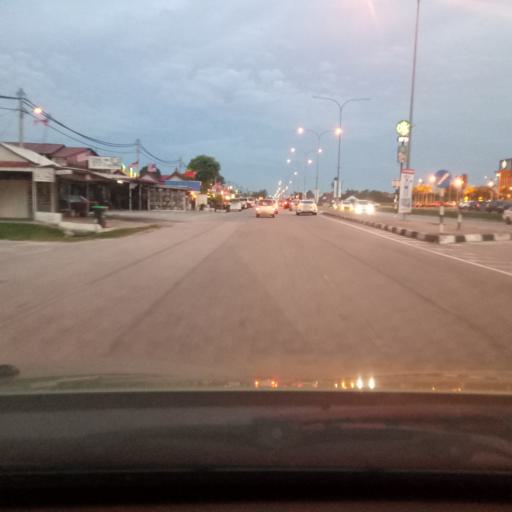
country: MY
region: Kedah
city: Alor Setar
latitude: 6.0971
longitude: 100.3757
